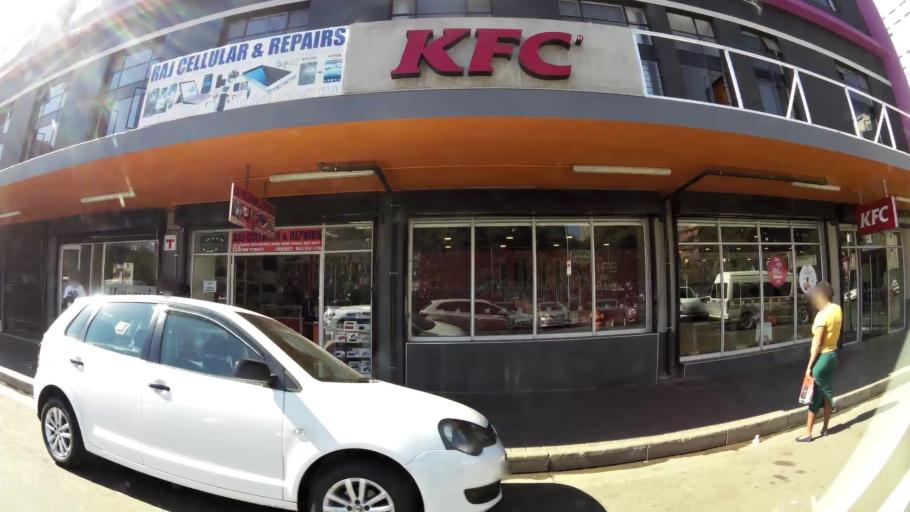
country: ZA
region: Gauteng
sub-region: City of Johannesburg Metropolitan Municipality
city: Johannesburg
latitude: -26.1990
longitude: 28.0531
